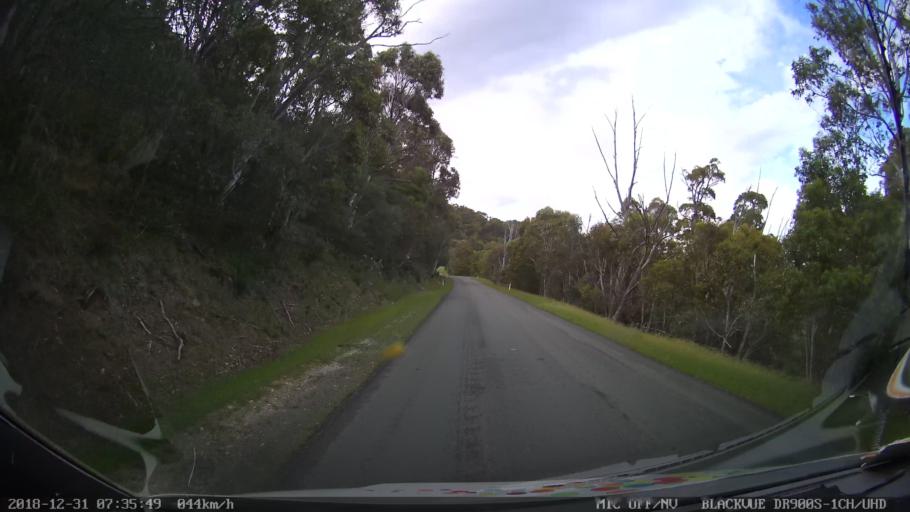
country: AU
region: New South Wales
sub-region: Snowy River
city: Jindabyne
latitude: -36.3369
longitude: 148.4439
